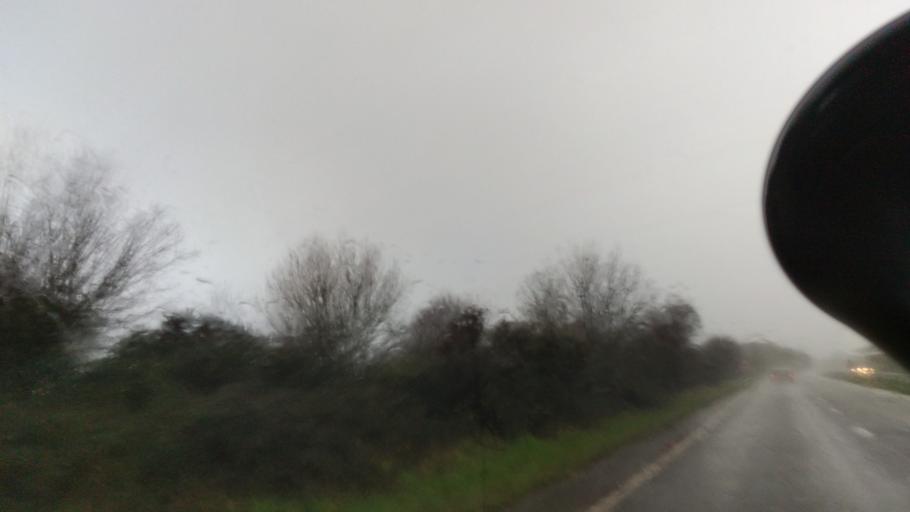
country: GB
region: England
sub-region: West Sussex
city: Walberton
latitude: 50.8529
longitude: -0.6248
